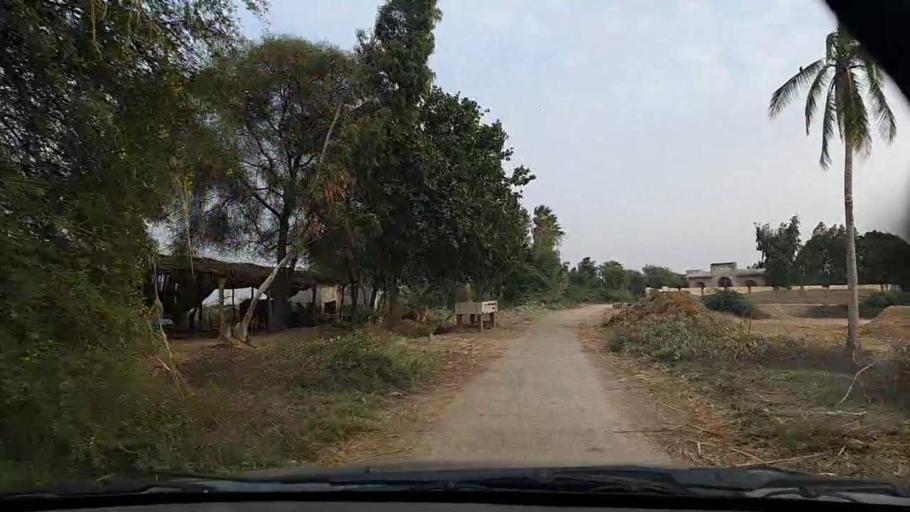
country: PK
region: Sindh
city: Thatta
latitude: 24.7329
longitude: 67.9364
